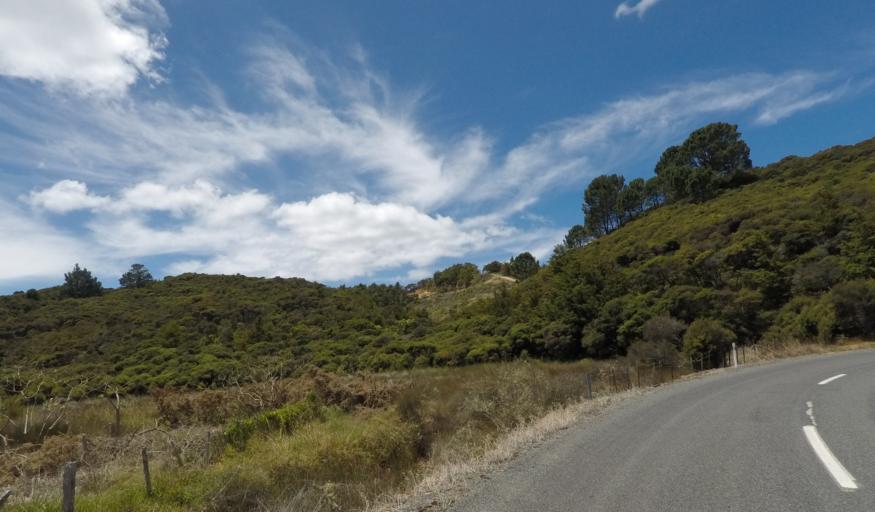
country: NZ
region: Northland
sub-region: Whangarei
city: Ngunguru
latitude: -35.5045
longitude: 174.4338
